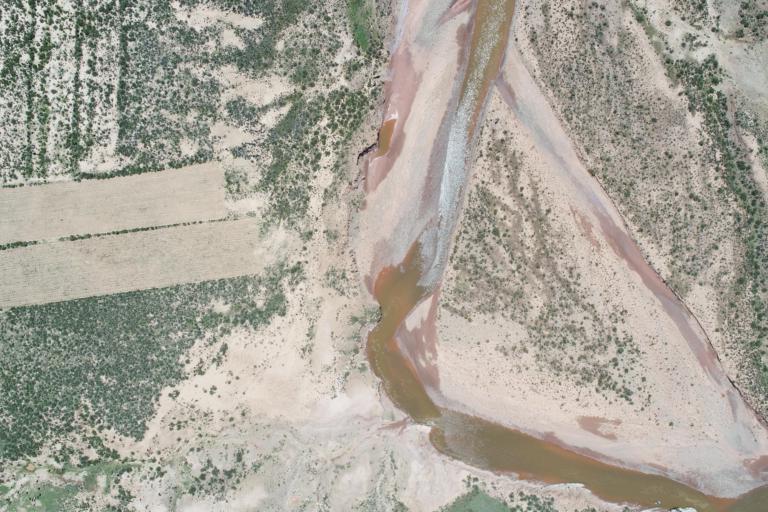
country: BO
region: La Paz
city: Curahuara de Carangas
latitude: -17.3198
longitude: -68.5127
